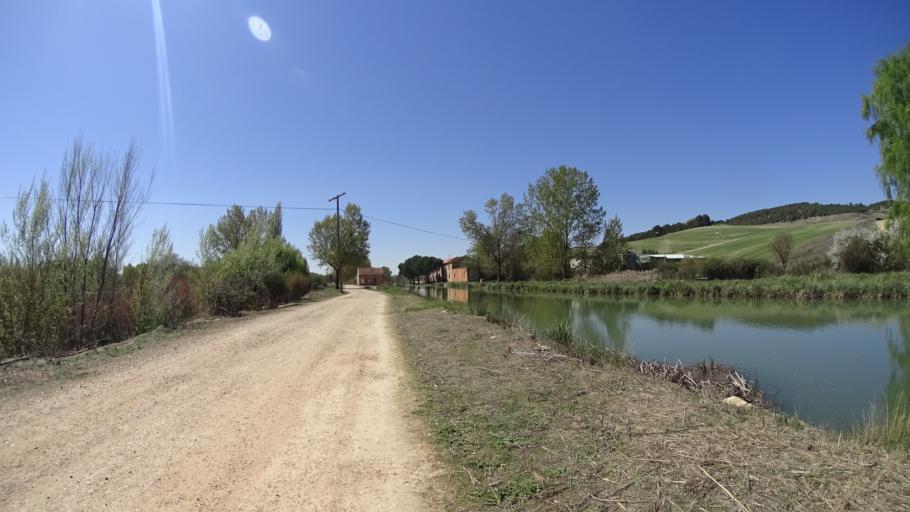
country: ES
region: Castille and Leon
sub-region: Provincia de Palencia
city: Duenas
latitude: 41.8872
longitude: -4.5350
